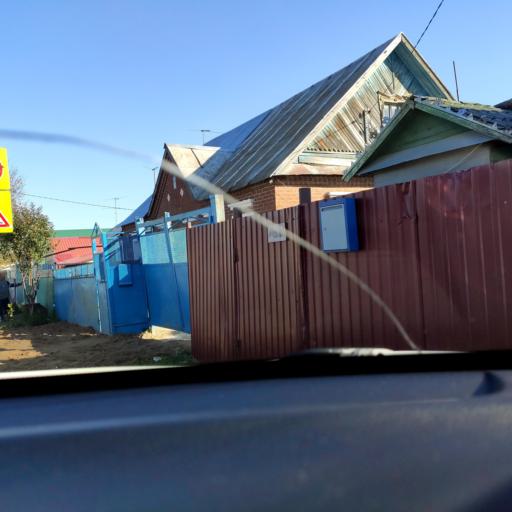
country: RU
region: Tatarstan
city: Vysokaya Gora
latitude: 55.8519
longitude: 49.2323
